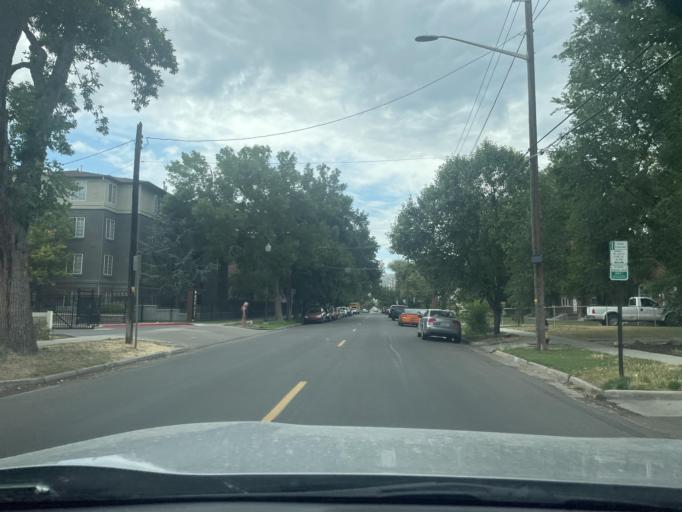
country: US
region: Utah
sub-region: Salt Lake County
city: South Salt Lake
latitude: 40.7373
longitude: -111.8939
